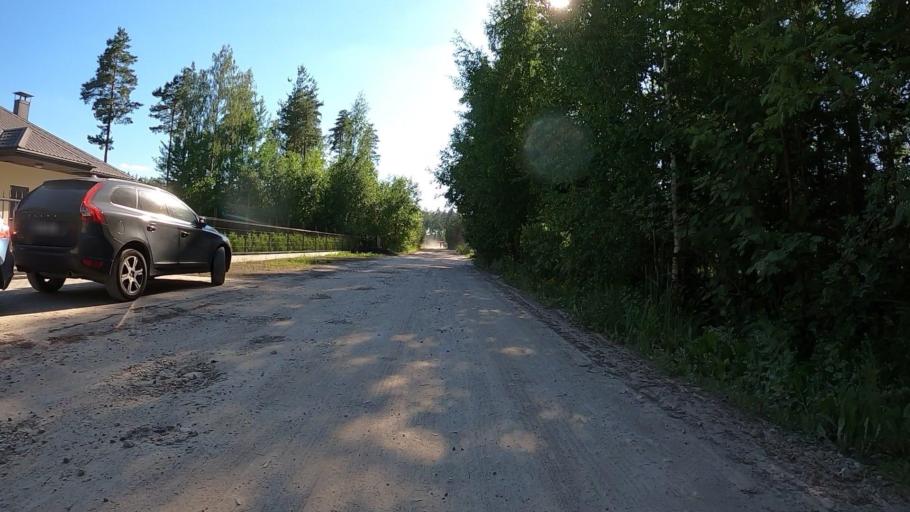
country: LV
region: Stopini
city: Ulbroka
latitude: 56.8757
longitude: 24.2839
